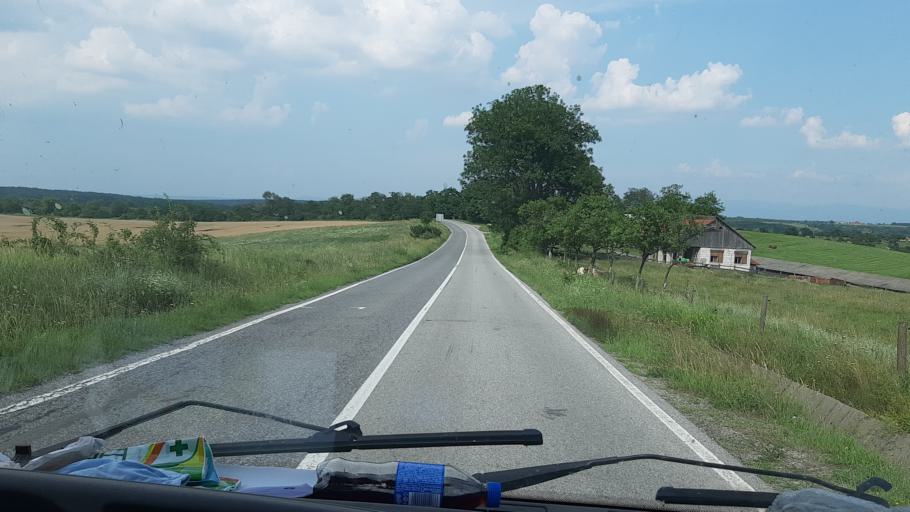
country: RO
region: Caras-Severin
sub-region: Comuna Farliug
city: Farliug
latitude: 45.5505
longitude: 21.8724
